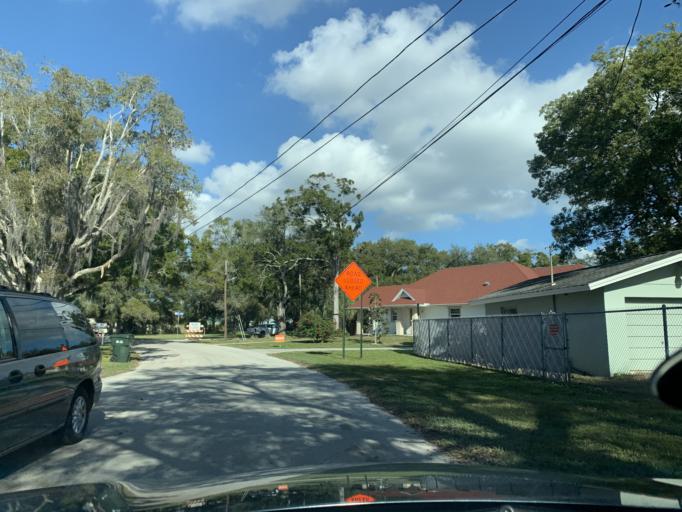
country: US
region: Florida
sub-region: Pinellas County
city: Belleair
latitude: 27.9264
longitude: -82.7942
